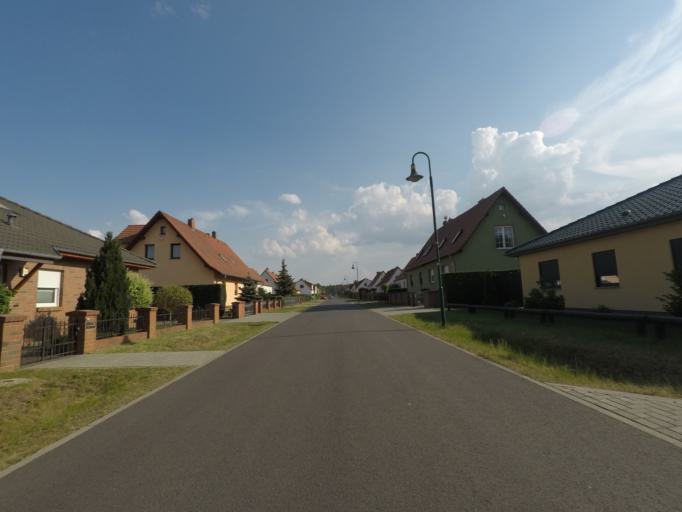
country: DE
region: Brandenburg
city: Melchow
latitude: 52.8381
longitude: 13.7208
